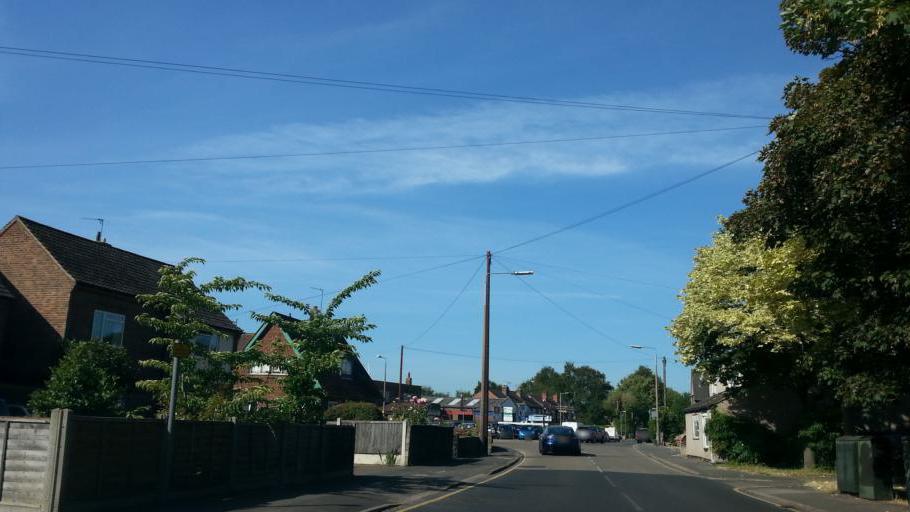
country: GB
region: England
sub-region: Derbyshire
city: Long Eaton
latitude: 52.9139
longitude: -1.2369
